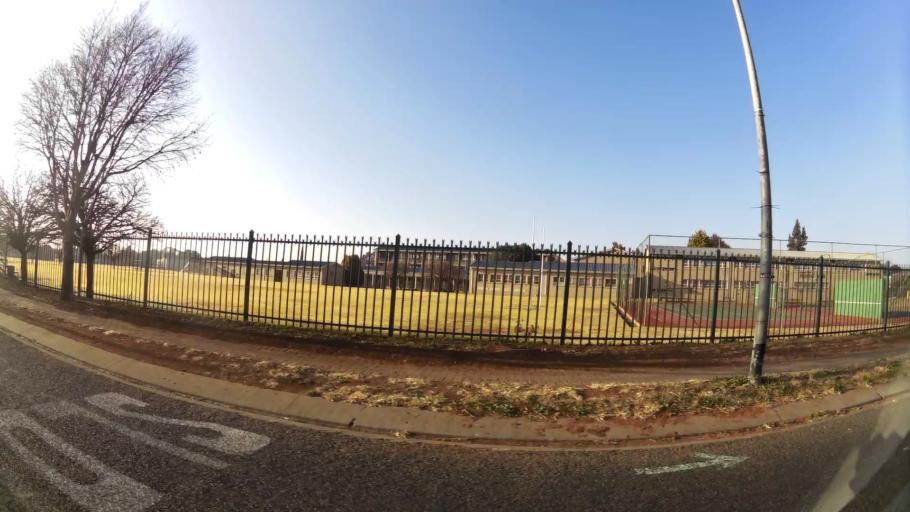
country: ZA
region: Orange Free State
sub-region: Mangaung Metropolitan Municipality
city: Bloemfontein
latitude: -29.1466
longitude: 26.1671
